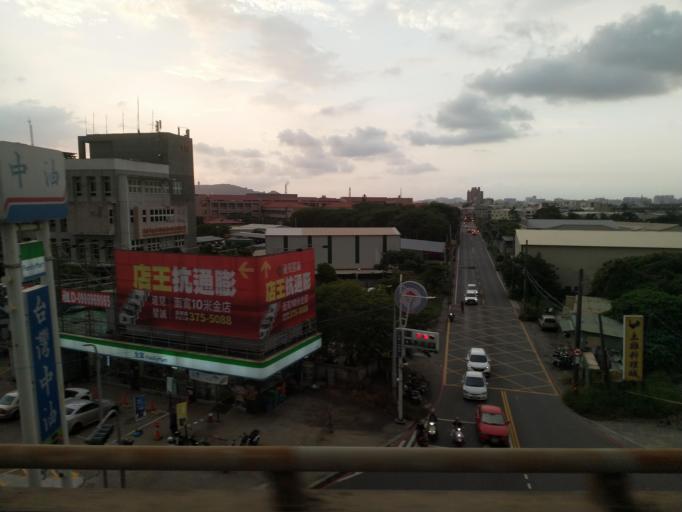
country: TW
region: Taiwan
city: Fengshan
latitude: 22.7018
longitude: 120.3596
